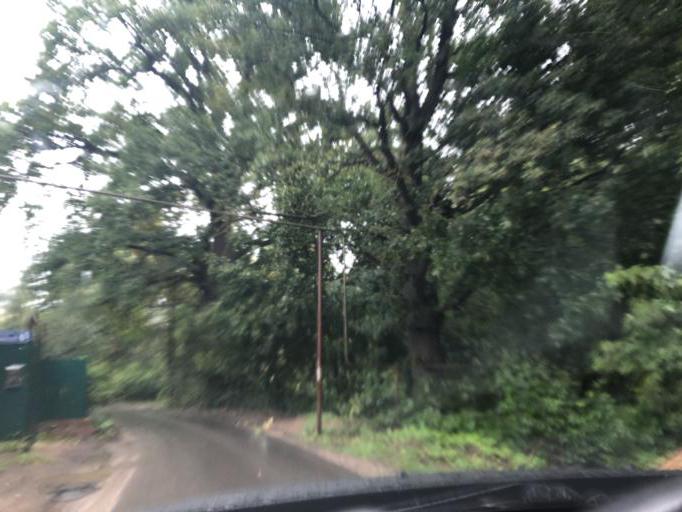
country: RU
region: Tula
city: Gorelki
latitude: 54.2548
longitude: 37.6132
